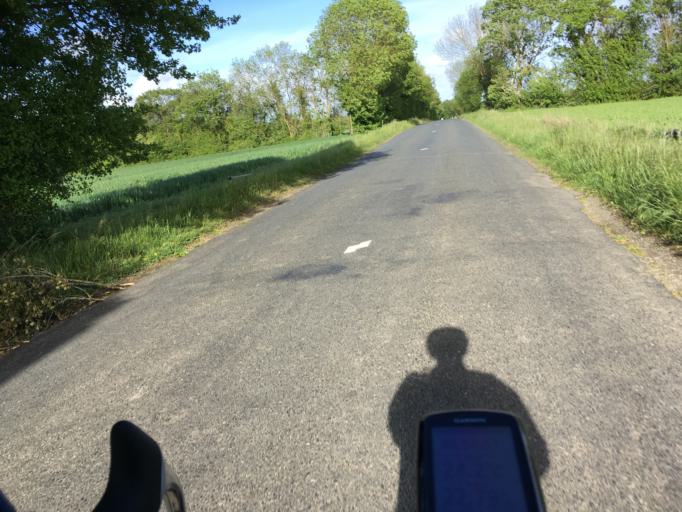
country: FR
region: Poitou-Charentes
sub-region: Departement de la Charente-Maritime
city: Verines
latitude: 46.1692
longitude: -0.8825
